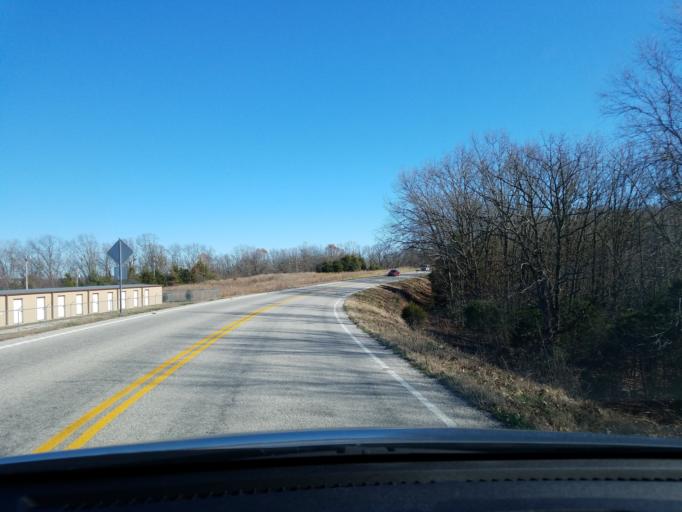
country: US
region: Missouri
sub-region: Taney County
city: Hollister
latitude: 36.5255
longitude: -93.2830
